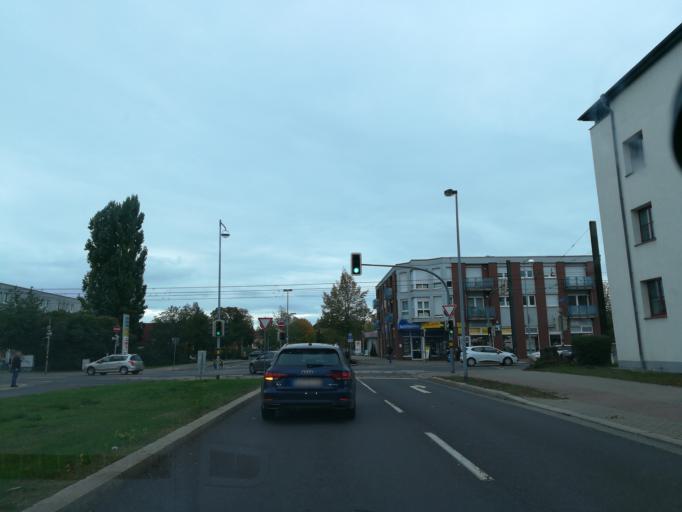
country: DE
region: Saxony-Anhalt
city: Magdeburg
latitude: 52.1202
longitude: 11.6601
